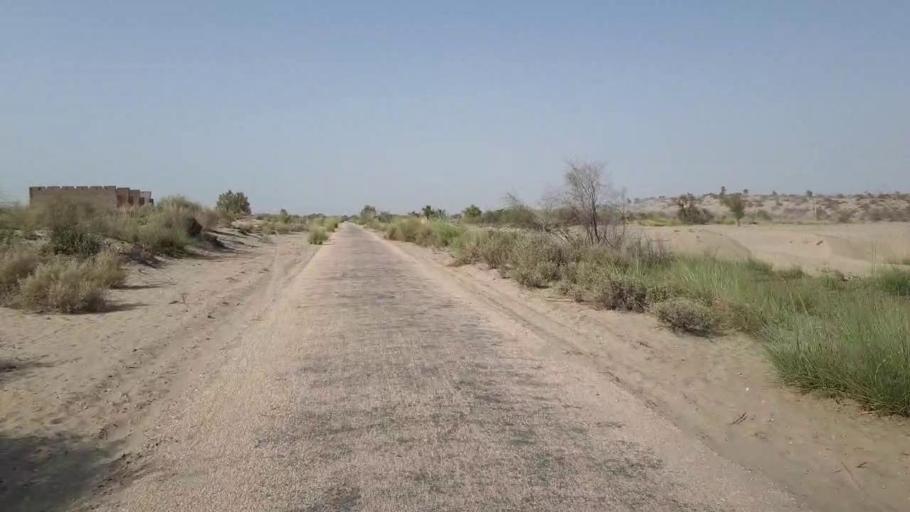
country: PK
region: Sindh
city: Jam Sahib
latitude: 26.5994
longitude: 68.9246
